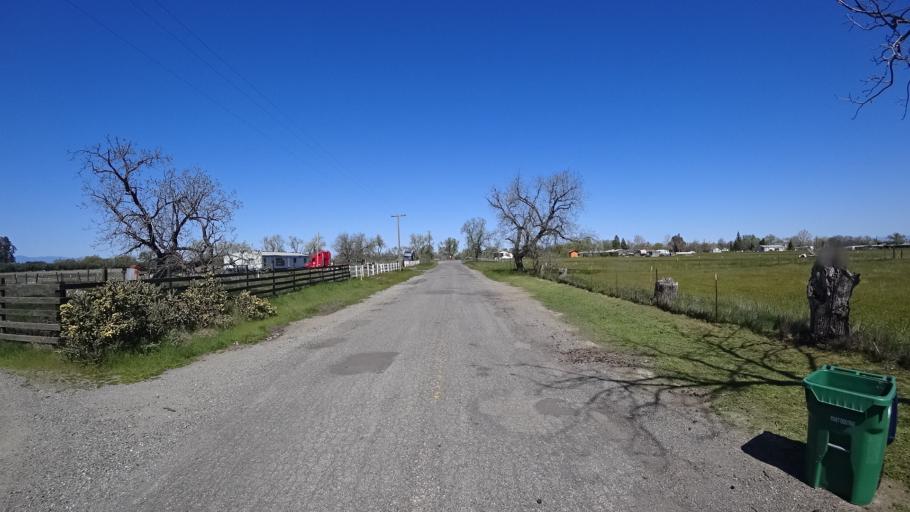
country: US
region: California
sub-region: Glenn County
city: Orland
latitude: 39.7820
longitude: -122.2476
